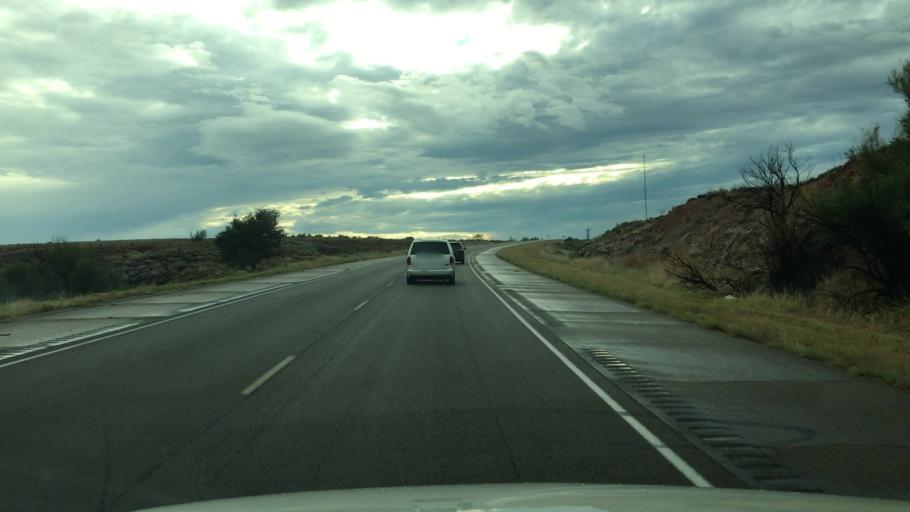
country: US
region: New Mexico
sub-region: Chaves County
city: Roswell
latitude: 33.3962
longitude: -104.3653
